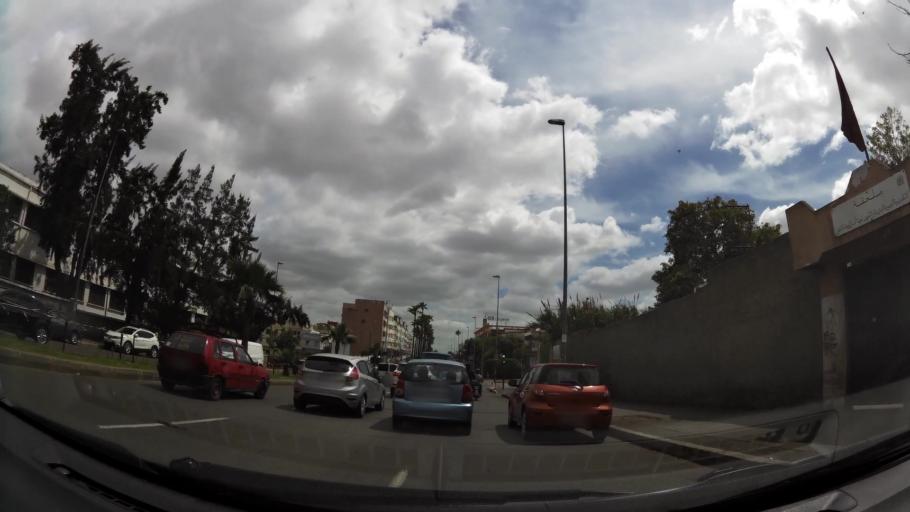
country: MA
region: Grand Casablanca
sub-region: Casablanca
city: Casablanca
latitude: 33.5619
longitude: -7.6127
